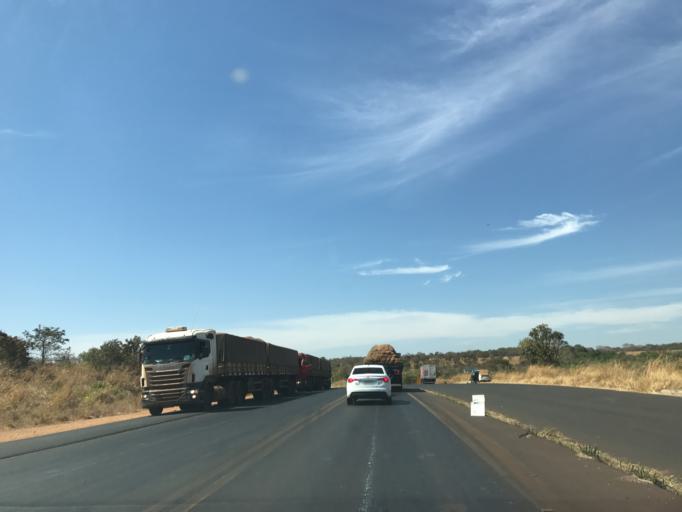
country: BR
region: Minas Gerais
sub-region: Monte Alegre De Minas
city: Monte Alegre de Minas
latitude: -18.8850
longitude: -49.0527
